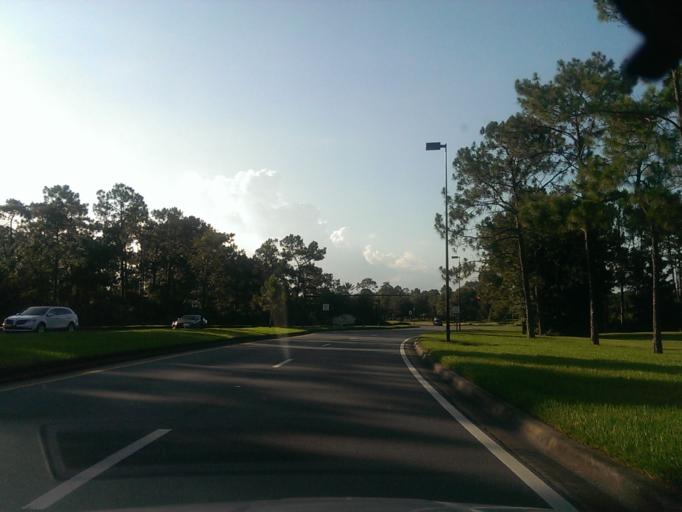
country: US
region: Florida
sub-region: Osceola County
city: Celebration
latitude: 28.3892
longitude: -81.5414
